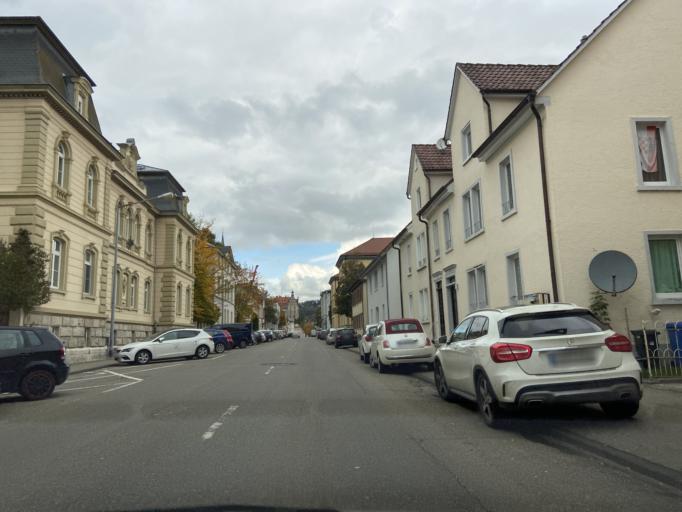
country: DE
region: Baden-Wuerttemberg
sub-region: Tuebingen Region
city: Sigmaringen
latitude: 48.0840
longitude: 9.2223
